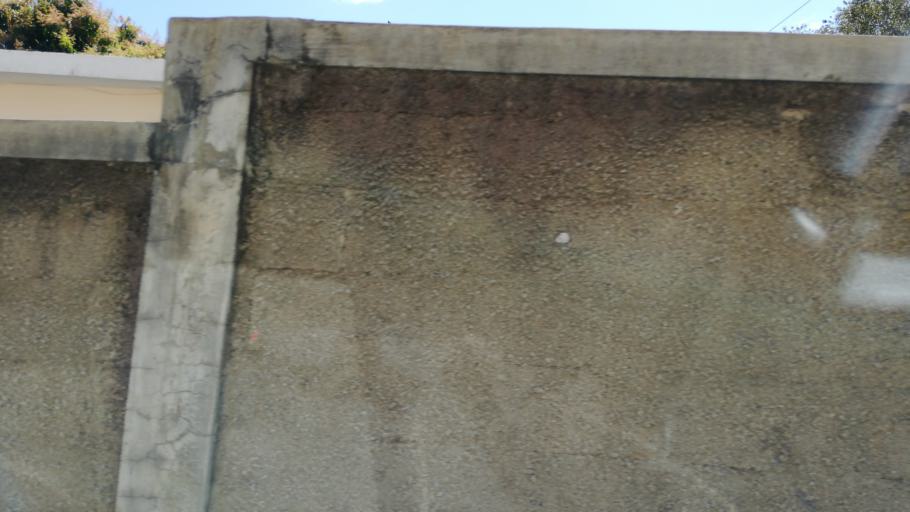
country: MU
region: Plaines Wilhems
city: Ebene
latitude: -20.2291
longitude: 57.4757
